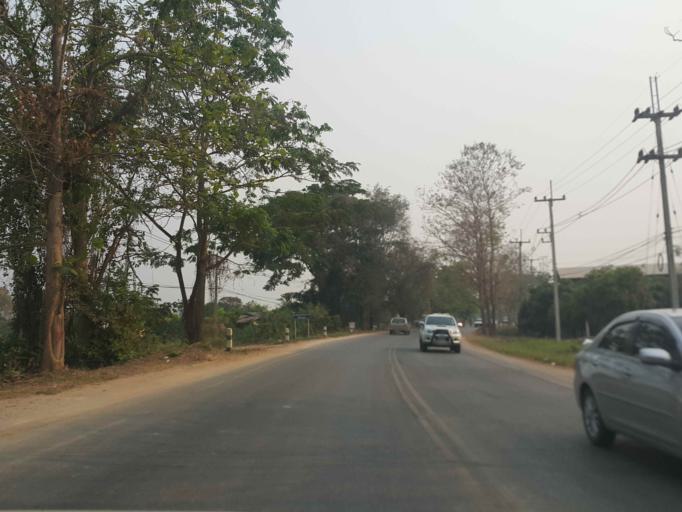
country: TH
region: Chiang Mai
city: Mae Taeng
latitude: 18.9923
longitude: 98.9783
